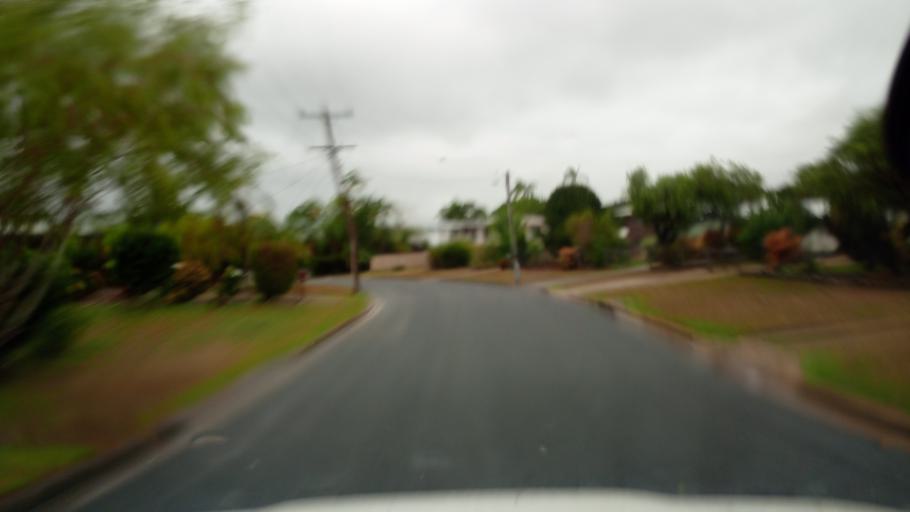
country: AU
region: Queensland
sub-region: Cairns
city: Woree
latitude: -16.9607
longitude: 145.7295
